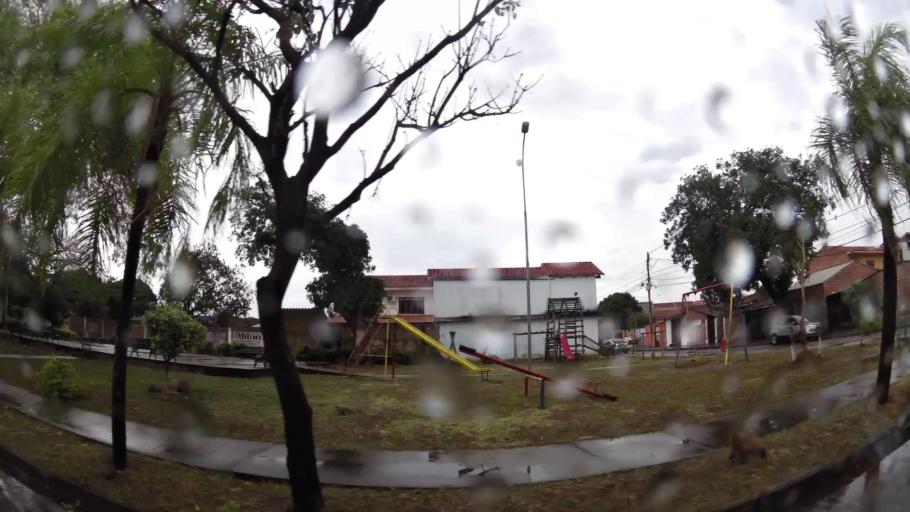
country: BO
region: Santa Cruz
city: Santa Cruz de la Sierra
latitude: -17.7670
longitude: -63.1547
